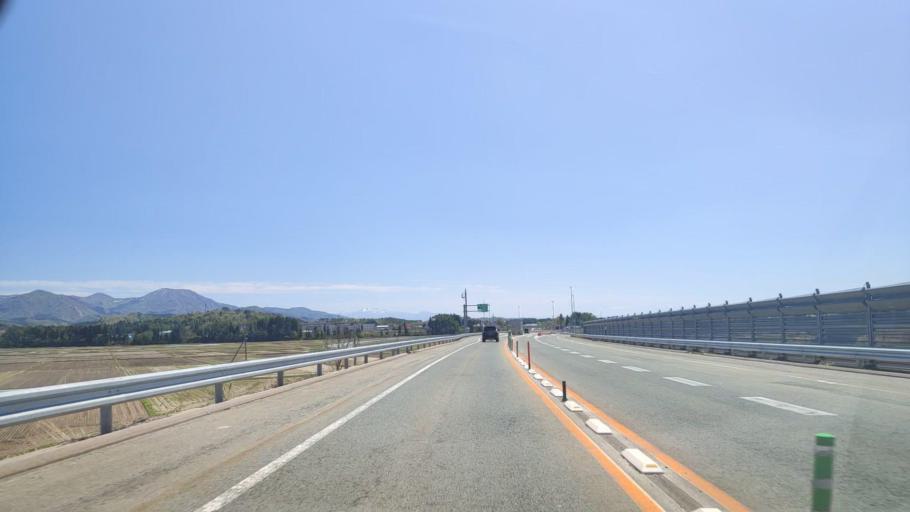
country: JP
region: Yamagata
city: Obanazawa
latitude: 38.6086
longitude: 140.3885
